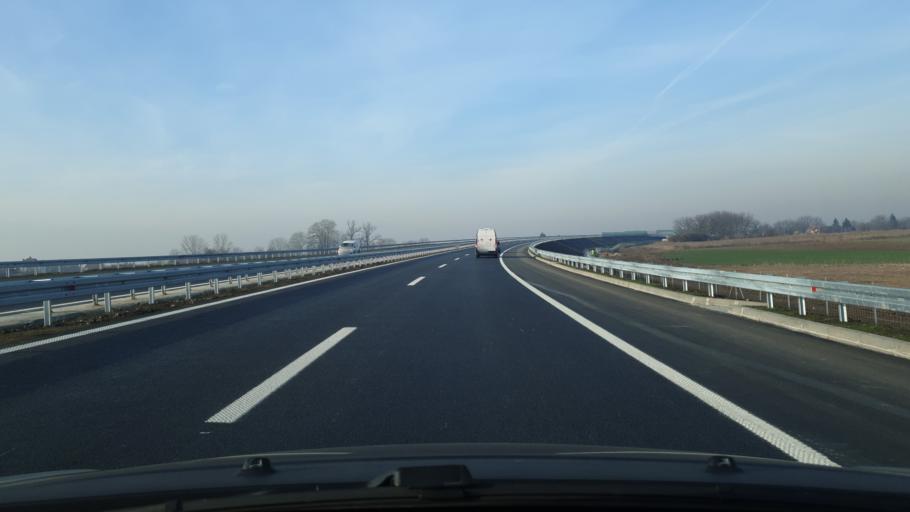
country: RS
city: Boljevci
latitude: 44.7284
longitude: 20.2485
